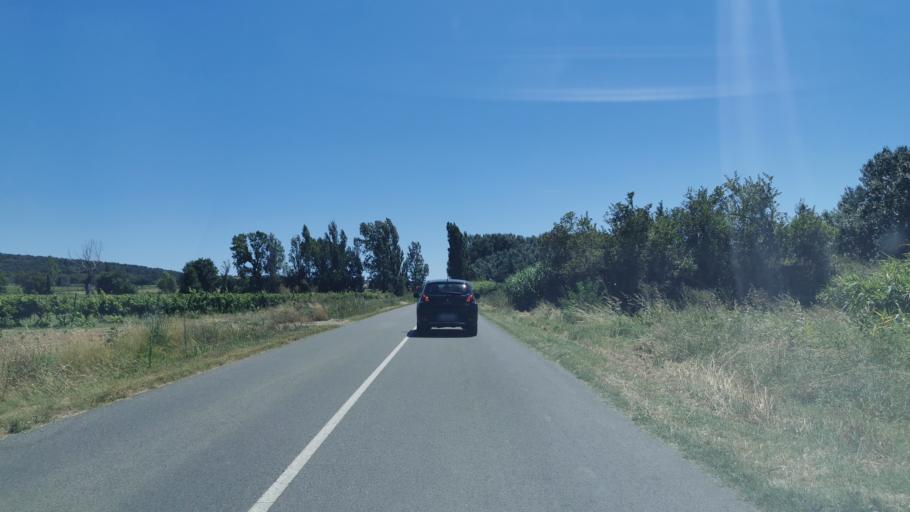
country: FR
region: Languedoc-Roussillon
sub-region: Departement de l'Aude
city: Vinassan
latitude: 43.2166
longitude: 3.0793
